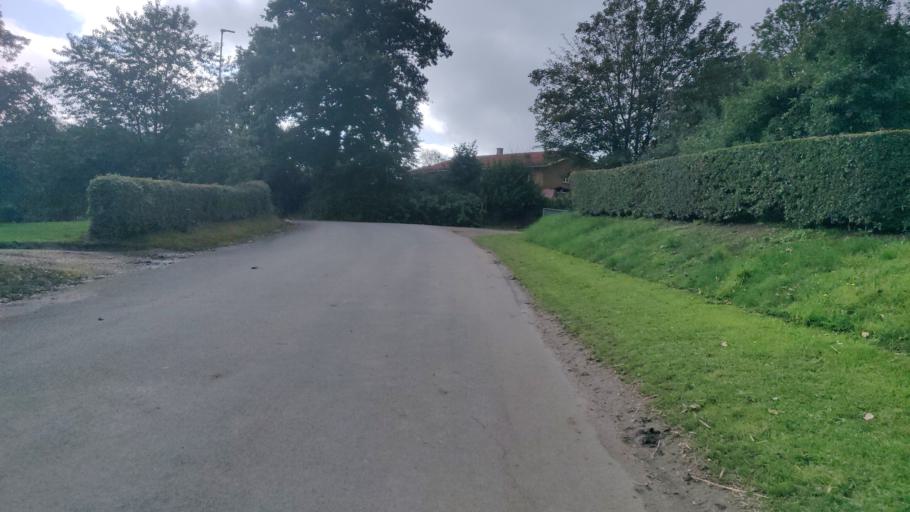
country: DK
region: South Denmark
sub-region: Kolding Kommune
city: Lunderskov
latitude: 55.5362
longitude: 9.3801
